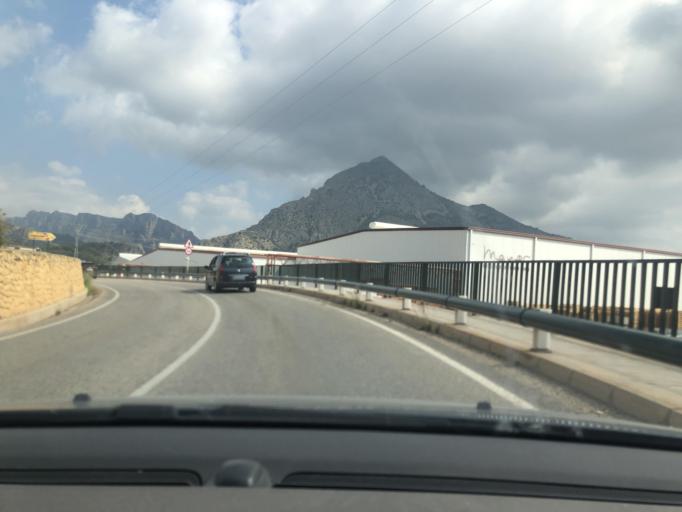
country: ES
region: Valencia
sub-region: Provincia de Alicante
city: Callosa d'En Sarria
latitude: 38.6536
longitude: -0.1076
